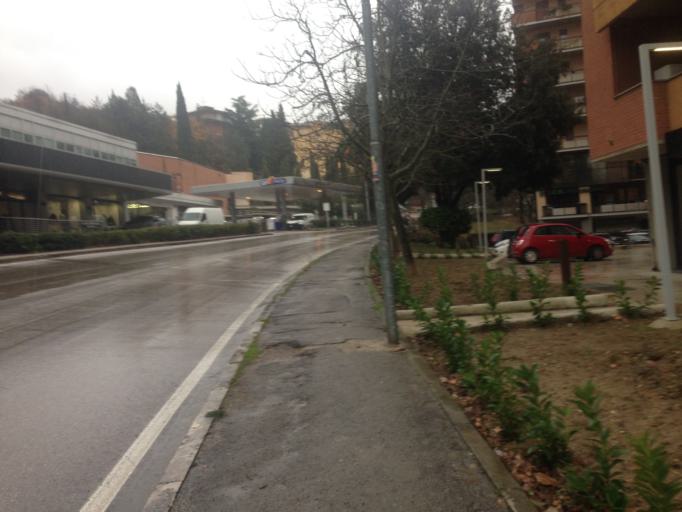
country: IT
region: Umbria
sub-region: Provincia di Perugia
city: Perugia
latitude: 43.1075
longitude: 12.3688
